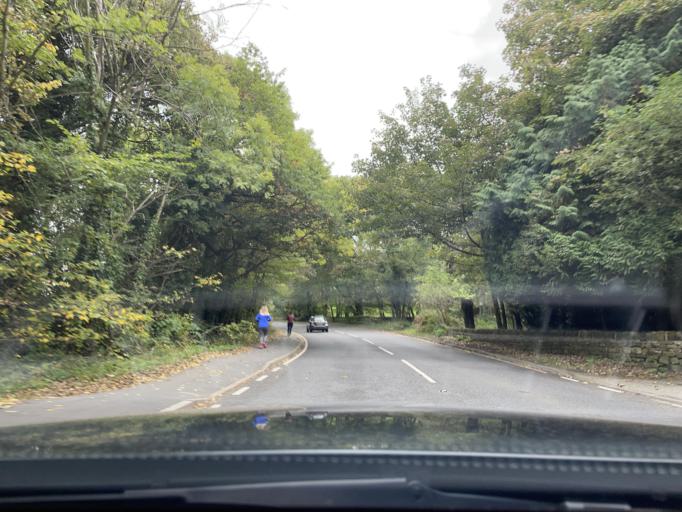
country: GB
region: England
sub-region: Sheffield
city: Bradfield
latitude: 53.3804
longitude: -1.5579
